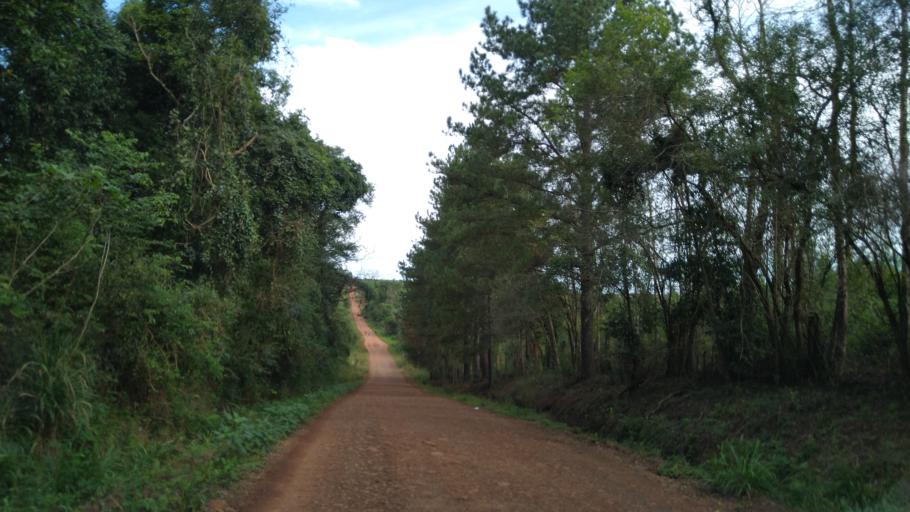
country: AR
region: Misiones
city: Capiovi
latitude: -26.9360
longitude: -55.0967
